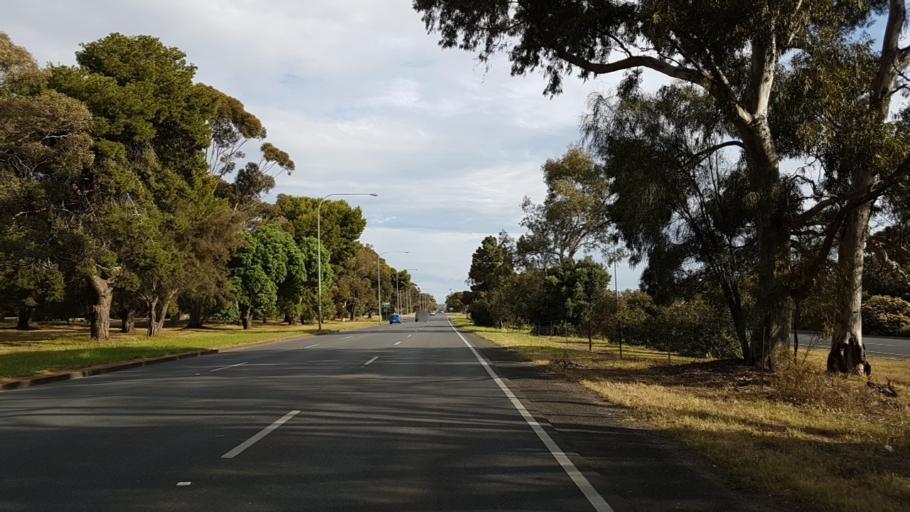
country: AU
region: South Australia
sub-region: Salisbury
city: Elizabeth
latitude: -34.7328
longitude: 138.6758
